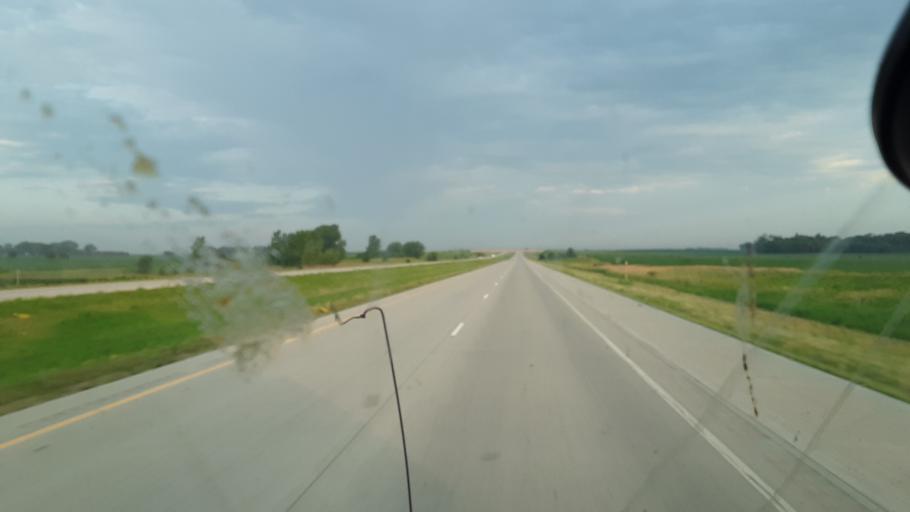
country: US
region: Minnesota
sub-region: Faribault County
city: Wells
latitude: 43.6653
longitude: -93.6162
